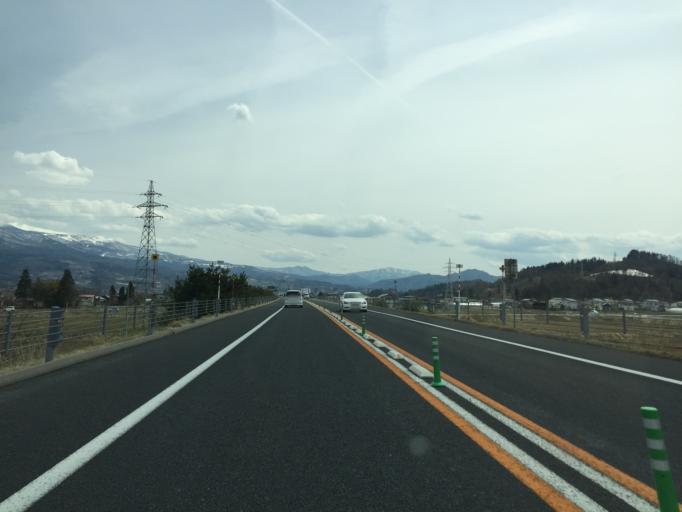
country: JP
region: Yamagata
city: Kaminoyama
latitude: 38.2225
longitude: 140.2810
